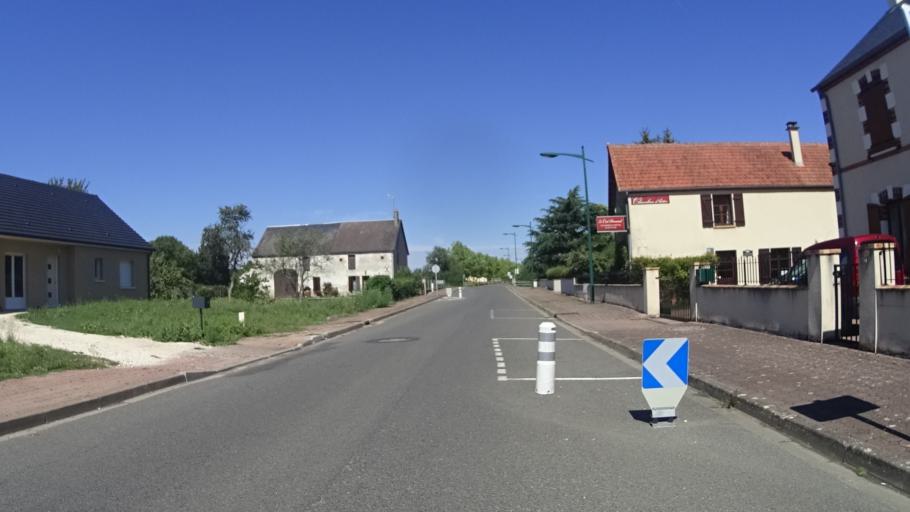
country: FR
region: Centre
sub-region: Departement du Cher
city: Belleville-sur-Loire
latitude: 47.5089
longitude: 2.8500
